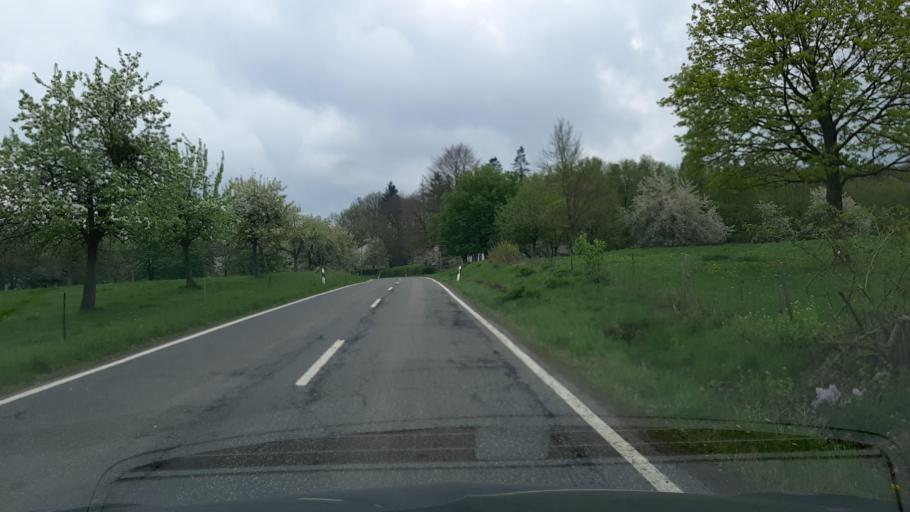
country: DE
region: Rheinland-Pfalz
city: Nortershausen
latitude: 50.2464
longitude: 7.5086
